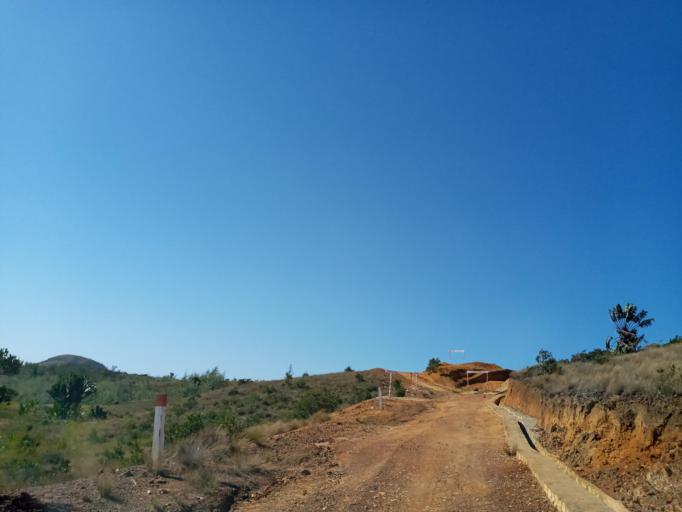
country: MG
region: Anosy
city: Fort Dauphin
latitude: -24.9126
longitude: 47.0873
